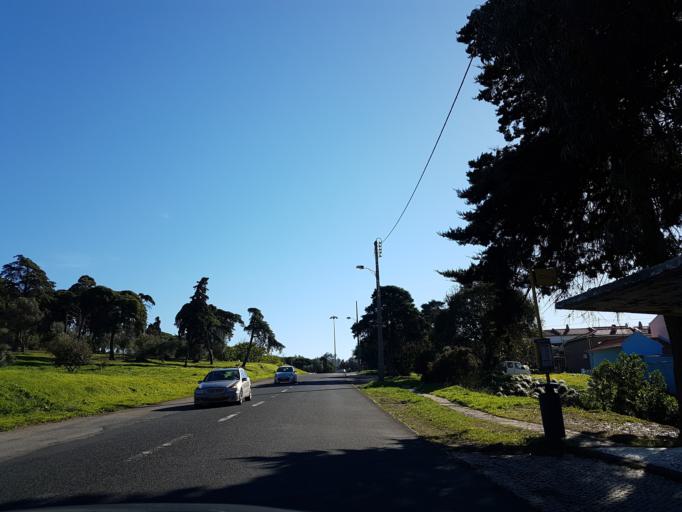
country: PT
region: Lisbon
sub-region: Oeiras
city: Alges
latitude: 38.7146
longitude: -9.2046
